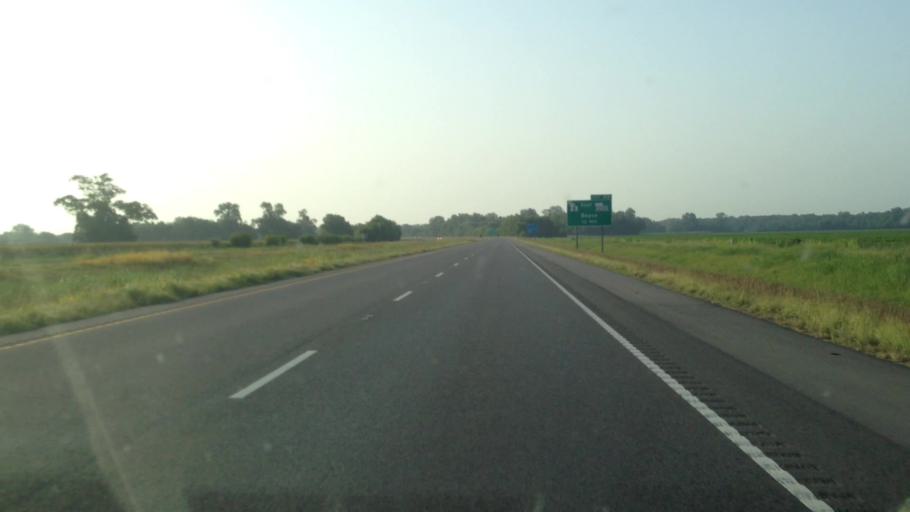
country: US
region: Louisiana
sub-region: Rapides Parish
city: Boyce
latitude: 31.3856
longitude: -92.6834
